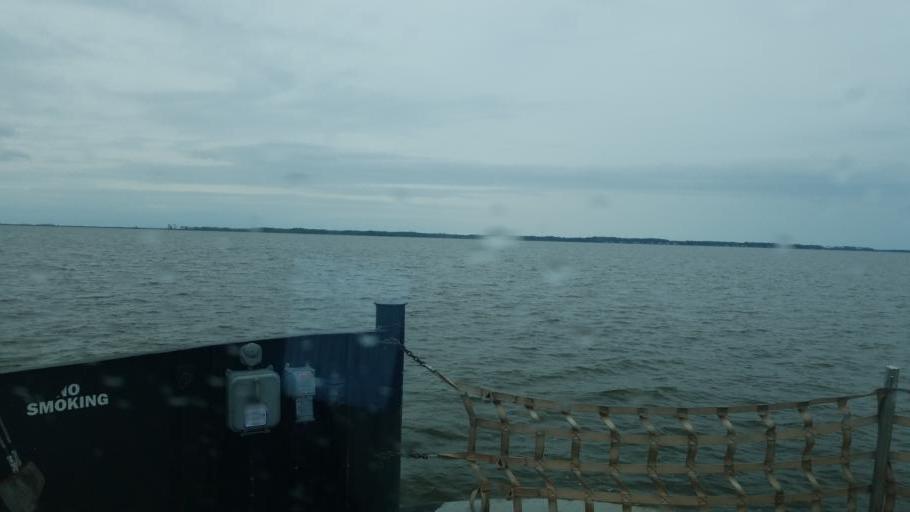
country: US
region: North Carolina
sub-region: Currituck County
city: Currituck
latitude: 36.4665
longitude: -75.9625
